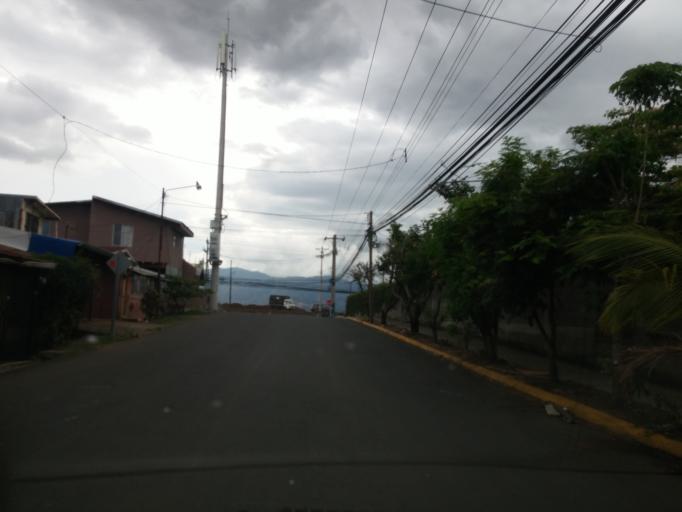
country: CR
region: Heredia
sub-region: Canton de Belen
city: San Antonio
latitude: 10.0014
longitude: -84.1947
